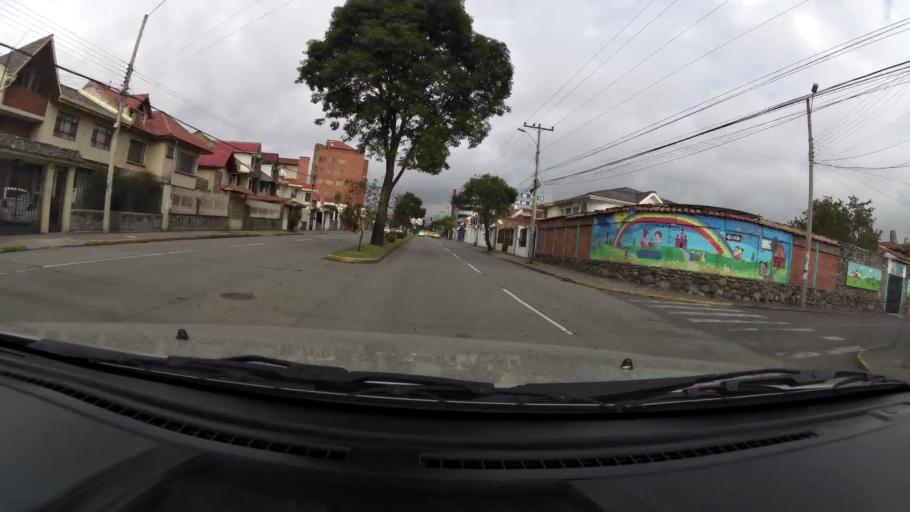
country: EC
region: Azuay
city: Cuenca
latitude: -2.9147
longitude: -78.9999
